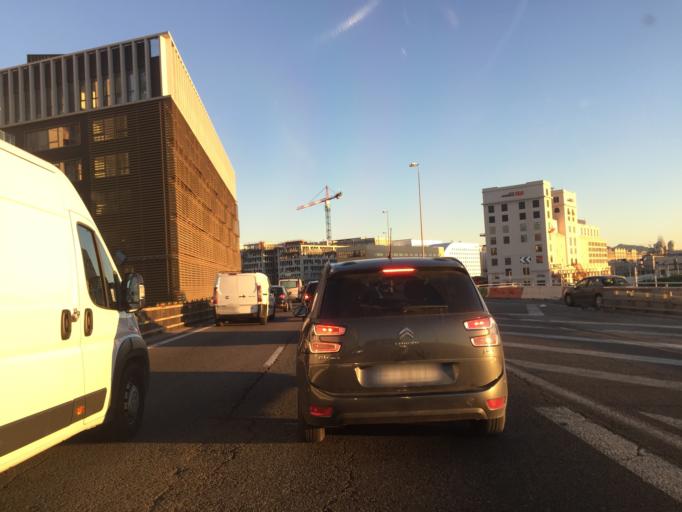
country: FR
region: Provence-Alpes-Cote d'Azur
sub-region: Departement des Bouches-du-Rhone
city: Marseille 03
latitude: 43.3133
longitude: 5.3662
